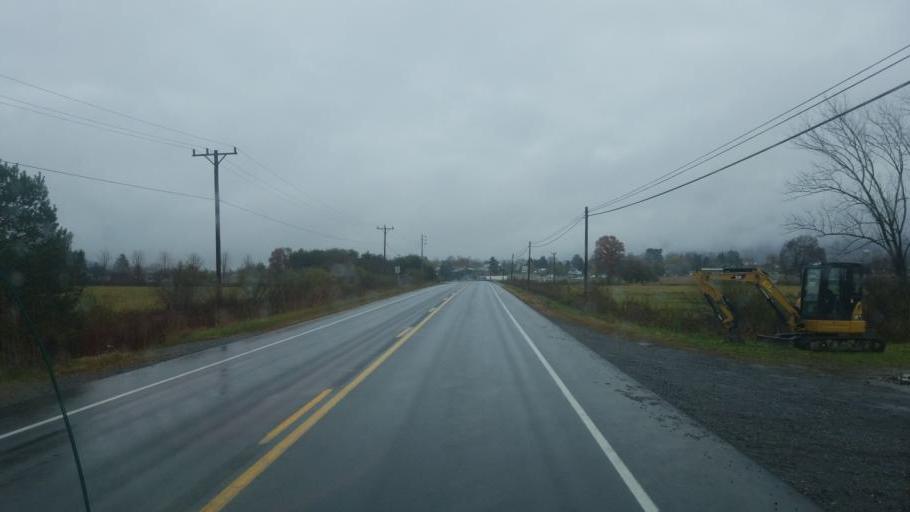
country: US
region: Pennsylvania
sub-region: Clinton County
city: Mill Hall
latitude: 41.0629
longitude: -77.6089
